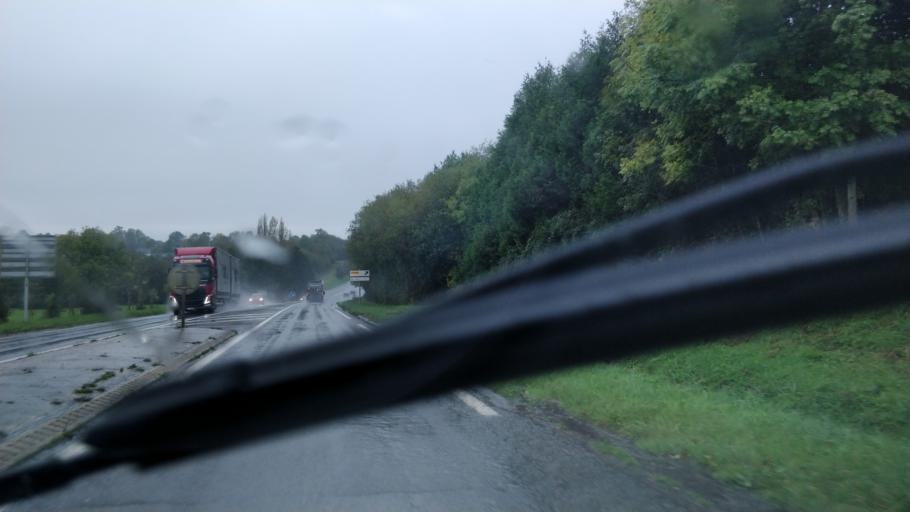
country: FR
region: Lower Normandy
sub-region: Departement de la Manche
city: Saint-Planchers
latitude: 48.8532
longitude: -1.5398
